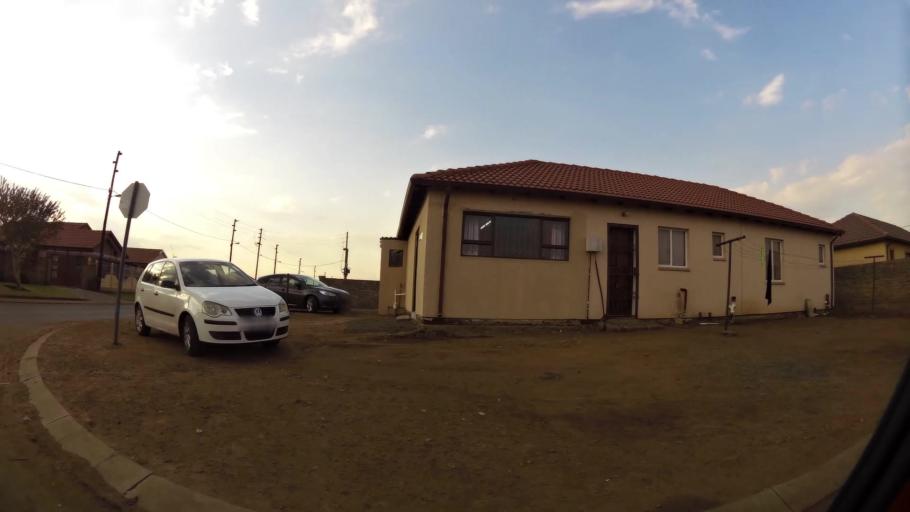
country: ZA
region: Gauteng
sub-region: Sedibeng District Municipality
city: Vanderbijlpark
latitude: -26.6129
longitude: 27.8129
